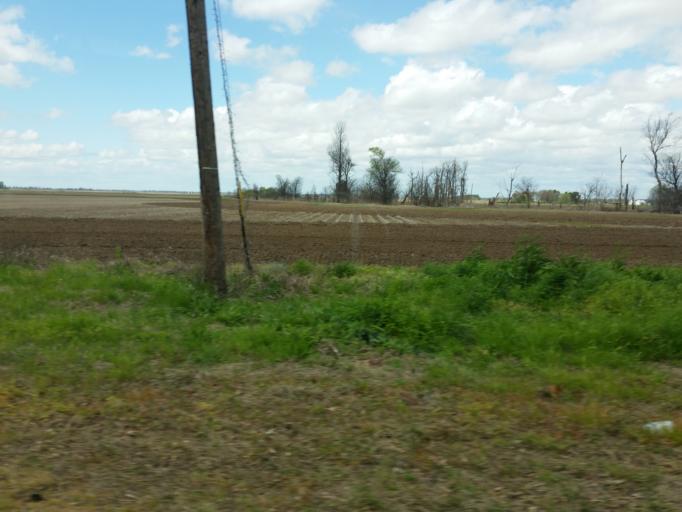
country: US
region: Arkansas
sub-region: Greene County
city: Paragould
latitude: 36.0663
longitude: -90.6726
